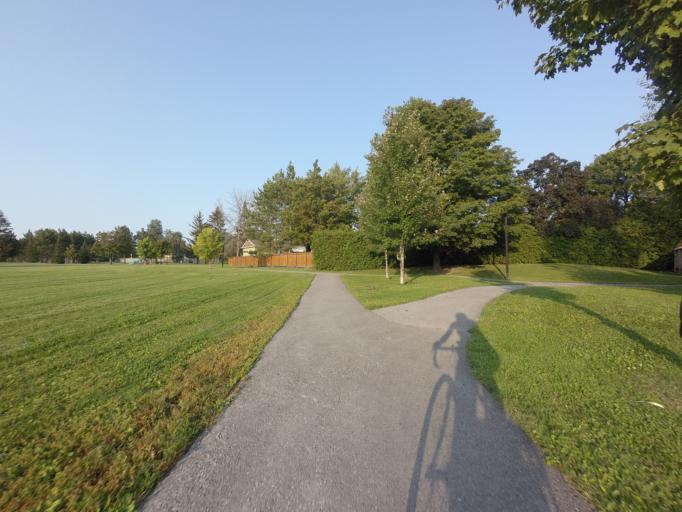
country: CA
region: Ontario
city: Bells Corners
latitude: 45.2891
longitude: -75.8777
